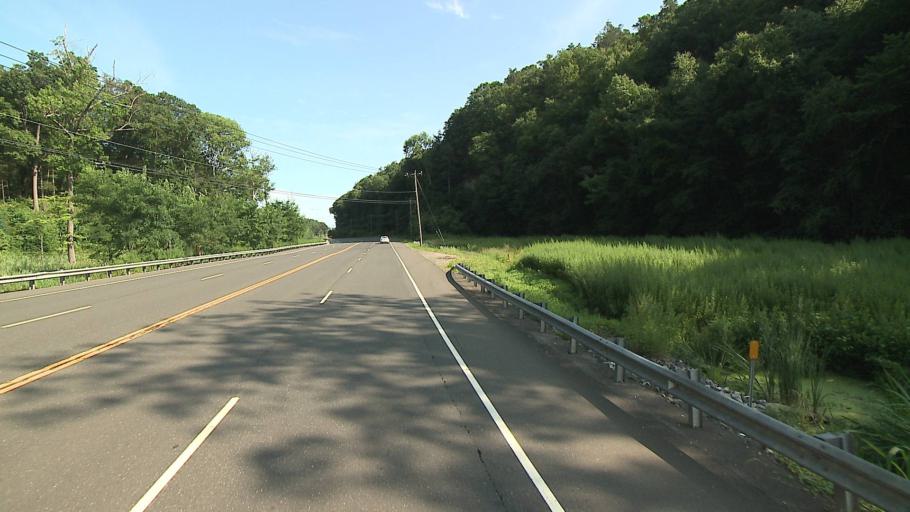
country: US
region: Connecticut
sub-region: Fairfield County
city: Danbury
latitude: 41.3586
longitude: -73.4719
